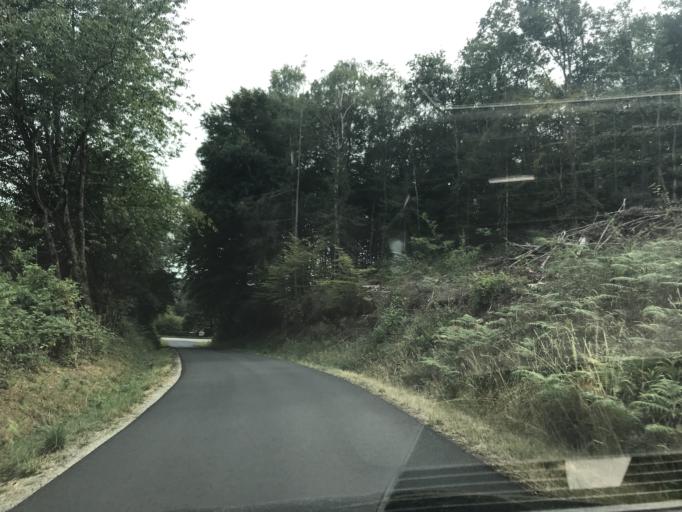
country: FR
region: Limousin
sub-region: Departement de la Correze
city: Neuvic
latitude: 45.3767
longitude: 2.2499
